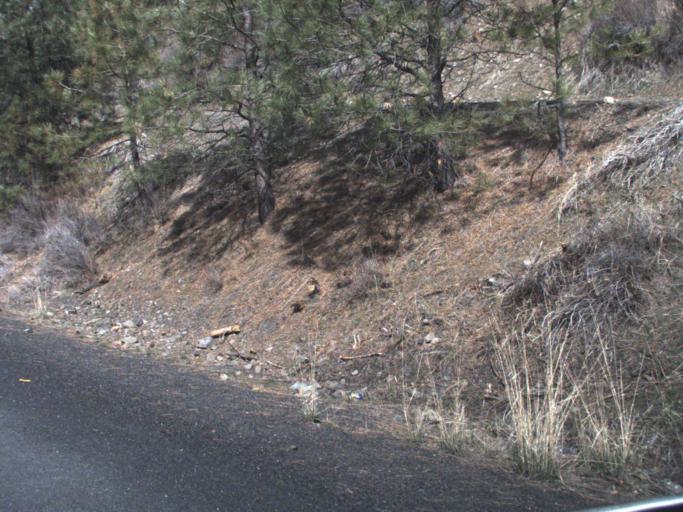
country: US
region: Washington
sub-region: Kittitas County
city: Cle Elum
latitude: 46.9036
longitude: -121.0200
